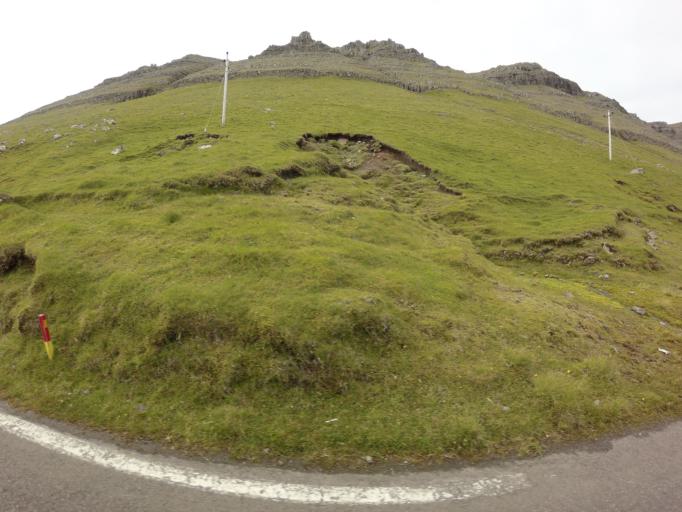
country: FO
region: Suduroy
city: Tvoroyri
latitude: 61.5777
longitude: -6.9393
